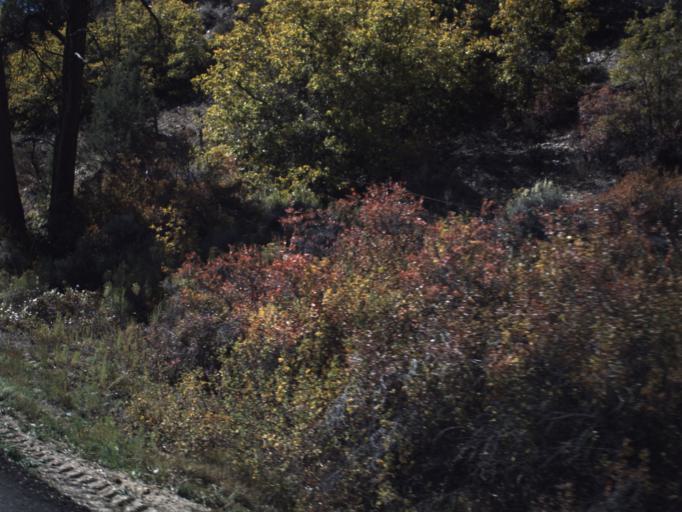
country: US
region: Utah
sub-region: Garfield County
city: Panguitch
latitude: 37.7175
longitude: -111.7832
